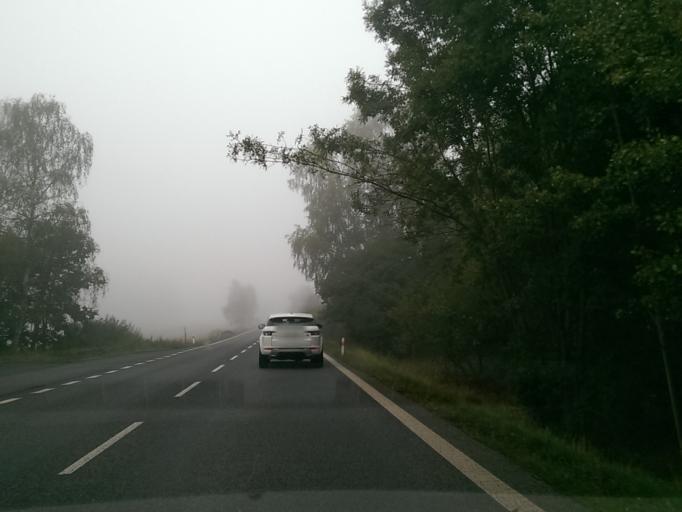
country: CZ
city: Doksy
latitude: 50.5980
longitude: 14.6030
